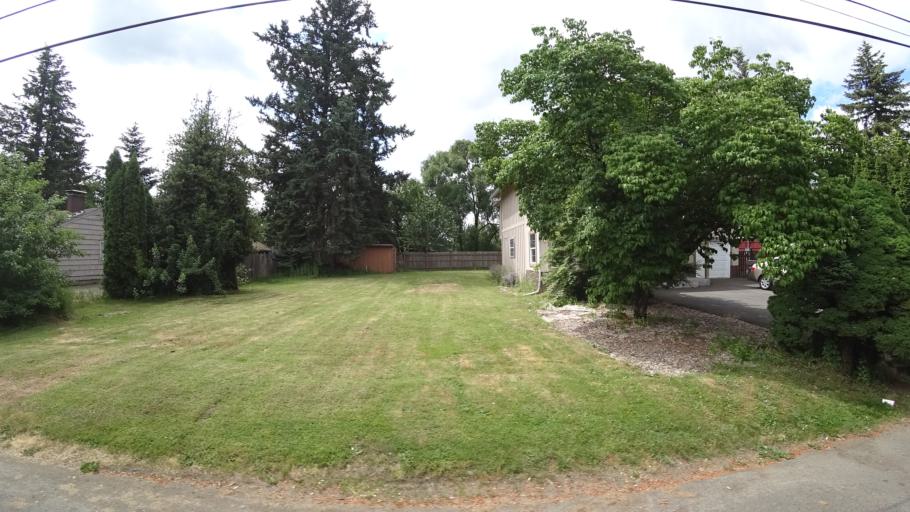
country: US
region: Oregon
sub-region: Multnomah County
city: Lents
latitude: 45.4954
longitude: -122.5265
